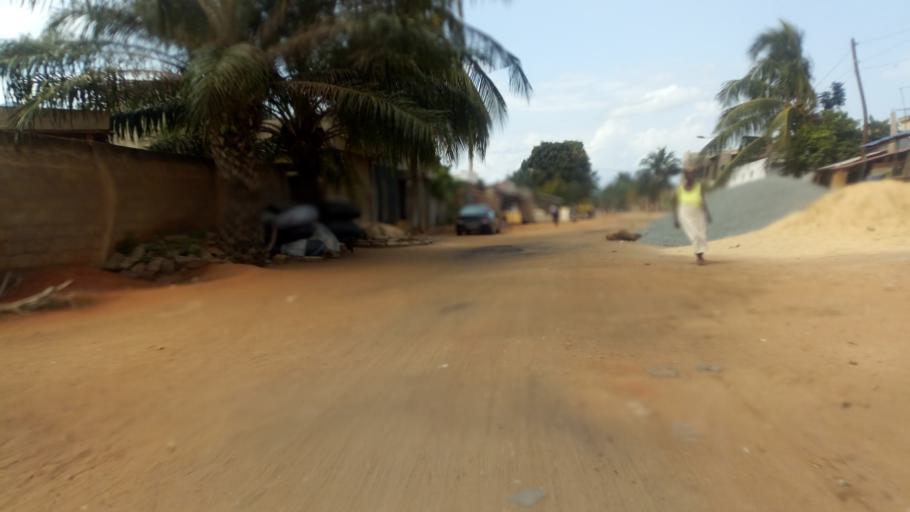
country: TG
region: Maritime
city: Lome
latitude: 6.2310
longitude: 1.1836
